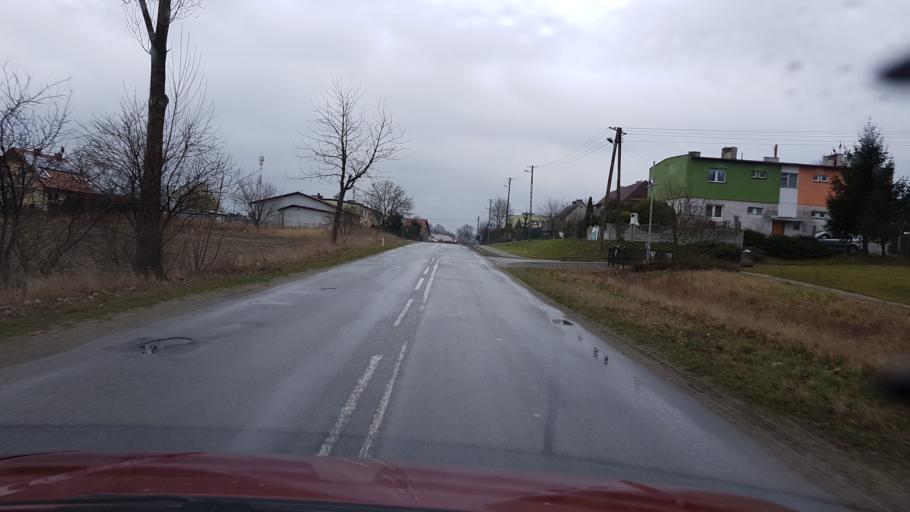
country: PL
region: West Pomeranian Voivodeship
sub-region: Powiat pyrzycki
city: Bielice
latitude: 53.2641
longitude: 14.6173
